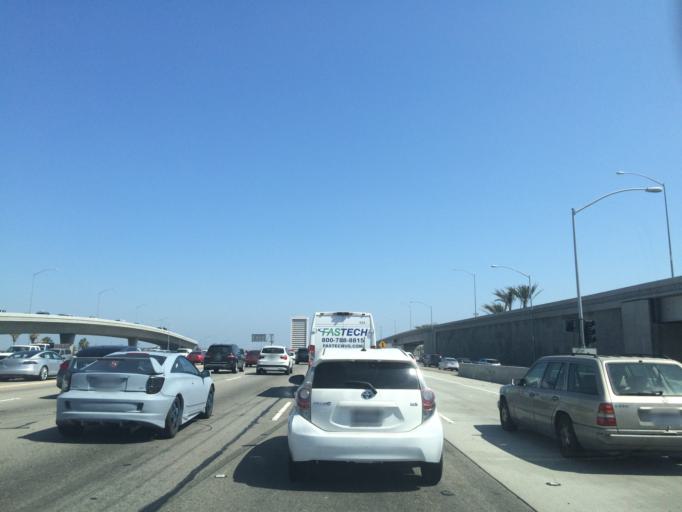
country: US
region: California
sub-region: Los Angeles County
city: Westwood, Los Angeles
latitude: 34.0569
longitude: -118.4533
